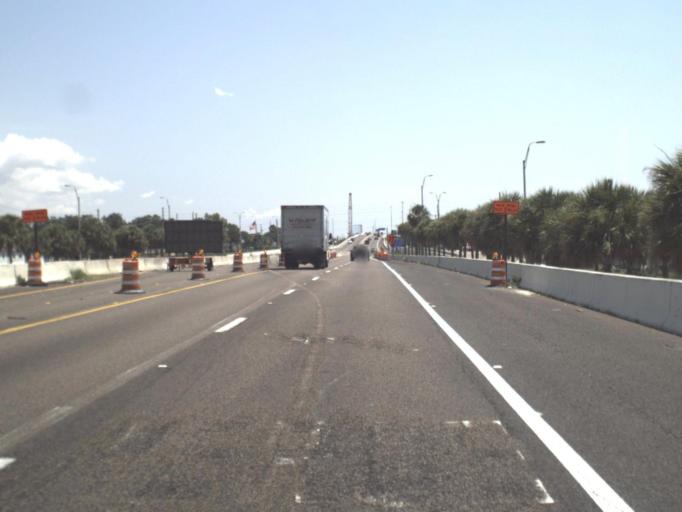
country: US
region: Florida
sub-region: Pinellas County
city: Safety Harbor
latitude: 27.9672
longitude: -82.7300
